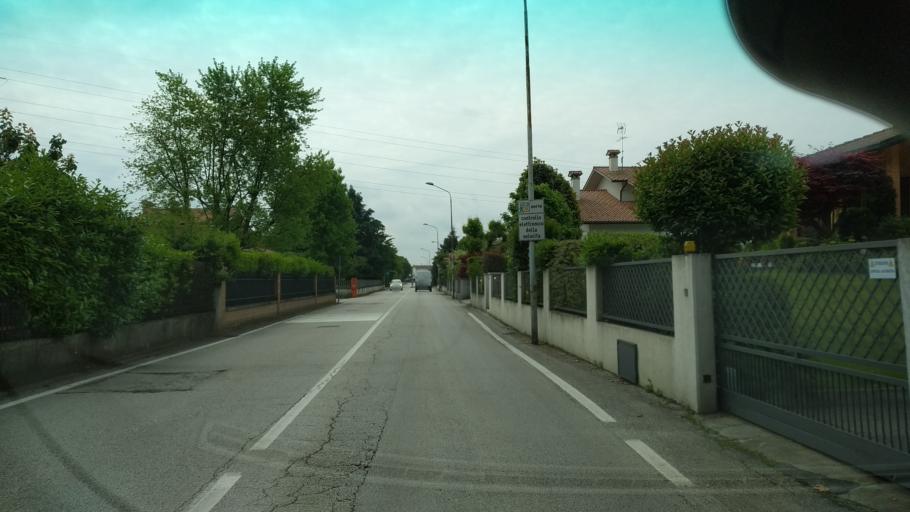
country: IT
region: Veneto
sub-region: Provincia di Vicenza
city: Motta
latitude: 45.5936
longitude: 11.5206
